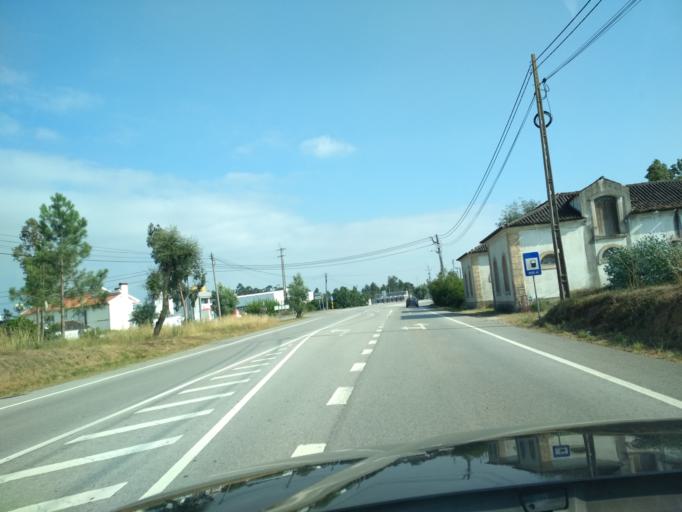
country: PT
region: Aveiro
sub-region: Mealhada
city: Pampilhosa do Botao
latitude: 40.3369
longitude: -8.4512
